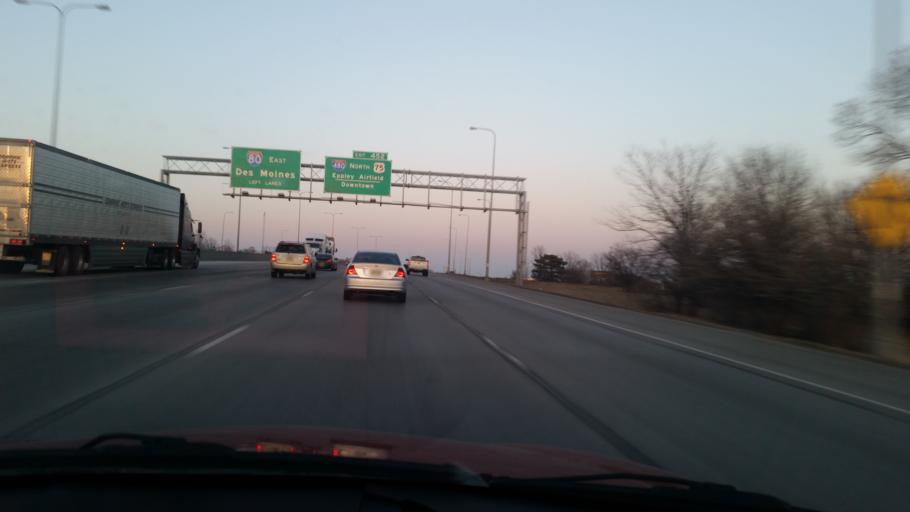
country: US
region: Nebraska
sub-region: Douglas County
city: Omaha
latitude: 41.2236
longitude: -95.9791
